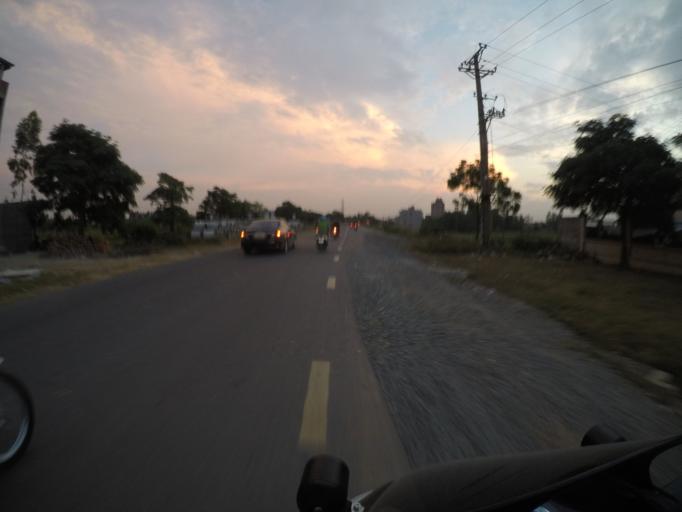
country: VN
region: Vinh Phuc
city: Phuc Yen
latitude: 21.2690
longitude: 105.7242
